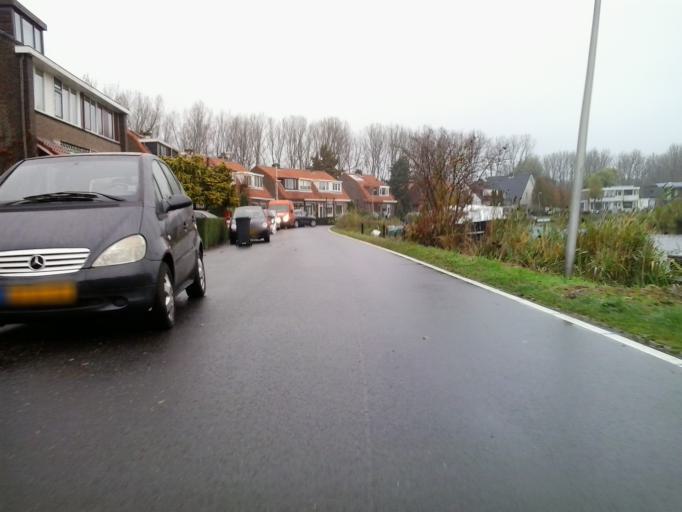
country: NL
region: South Holland
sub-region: Gemeente Lansingerland
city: Bergschenhoek
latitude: 51.9661
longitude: 4.5278
